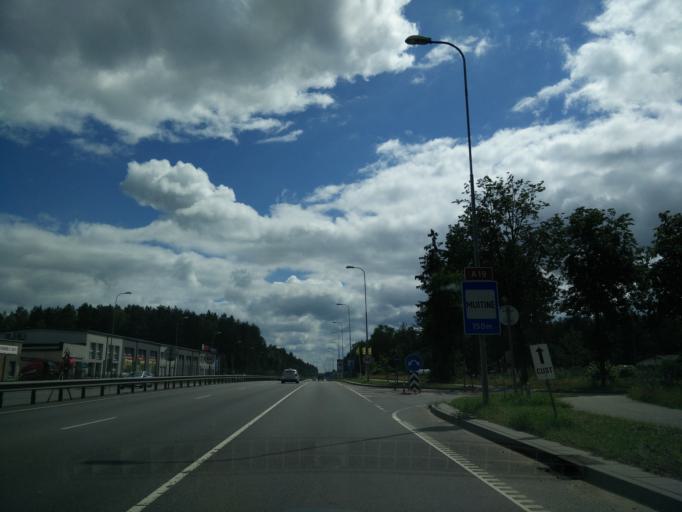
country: LT
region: Vilnius County
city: Pilaite
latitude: 54.6530
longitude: 25.1504
